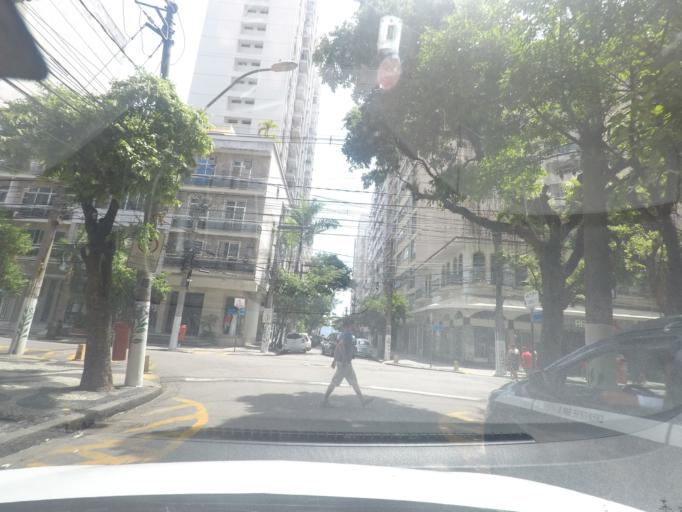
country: BR
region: Rio de Janeiro
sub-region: Niteroi
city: Niteroi
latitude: -22.9070
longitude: -43.1100
